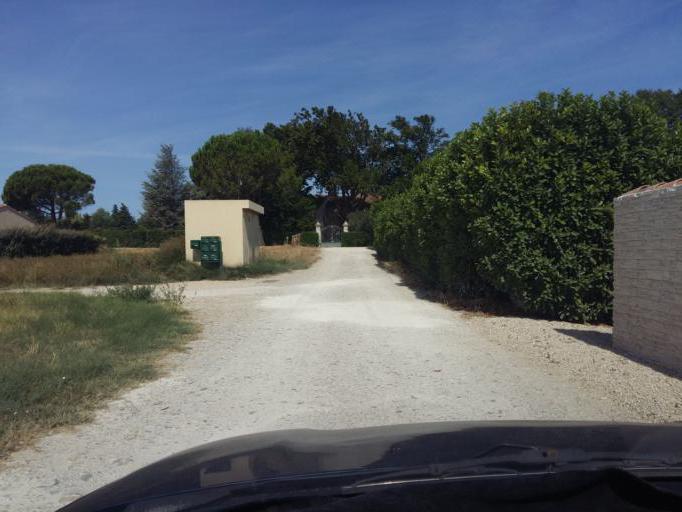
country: FR
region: Provence-Alpes-Cote d'Azur
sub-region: Departement du Vaucluse
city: Camaret-sur-Aigues
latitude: 44.1599
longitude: 4.8680
